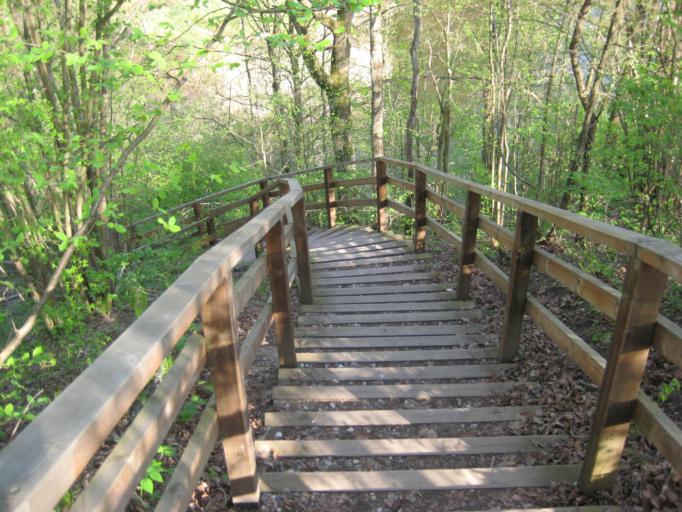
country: LT
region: Kauno apskritis
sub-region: Kauno rajonas
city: Karmelava
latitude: 54.8108
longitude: 24.1864
